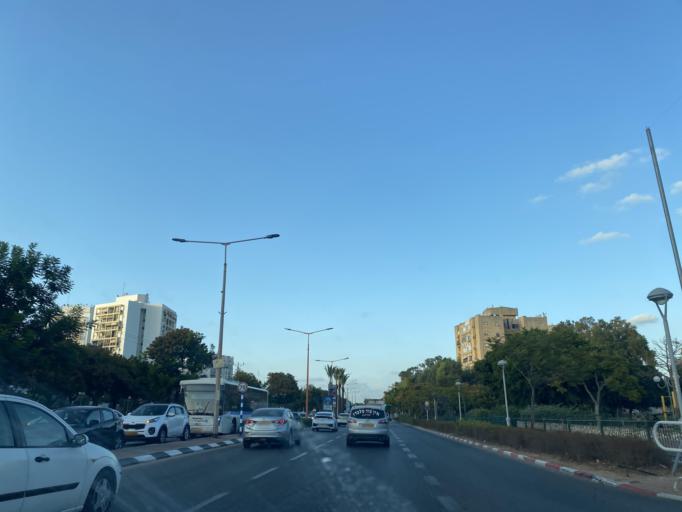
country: IL
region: Southern District
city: Ashdod
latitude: 31.7916
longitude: 34.6499
